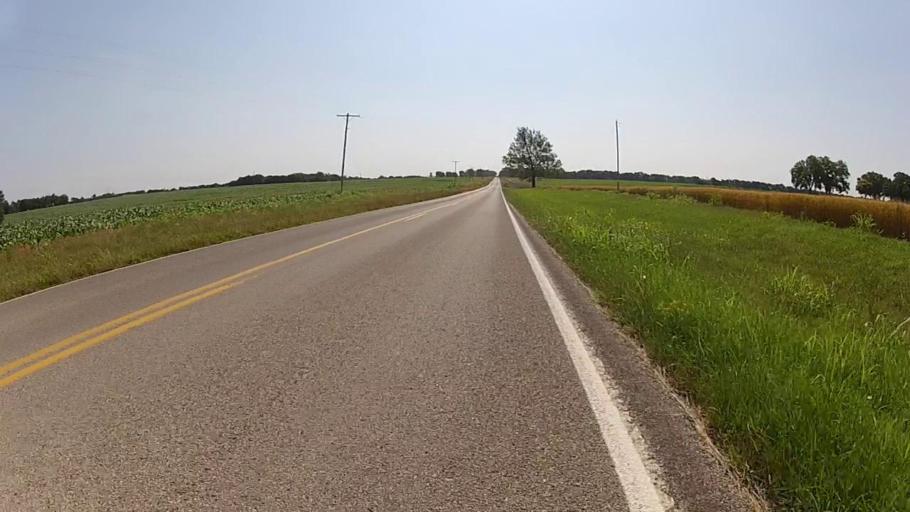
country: US
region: Kansas
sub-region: Montgomery County
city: Independence
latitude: 37.1931
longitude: -95.7505
